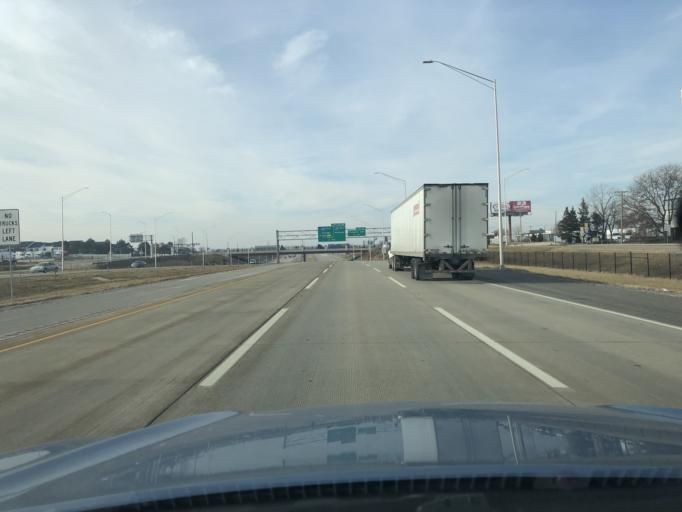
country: US
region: Illinois
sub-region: DuPage County
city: Wood Dale
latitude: 41.9838
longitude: -87.9759
